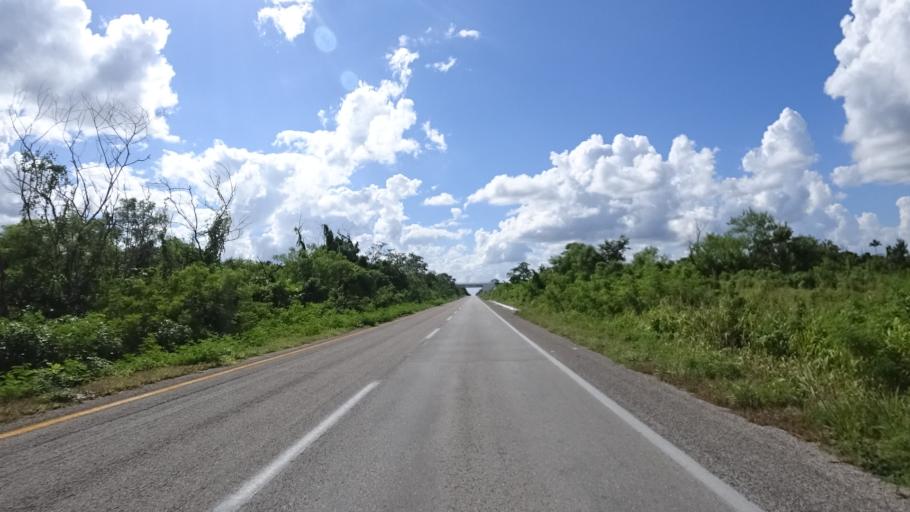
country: MX
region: Yucatan
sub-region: Kantunil
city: Kantunil
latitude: 20.7802
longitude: -88.9056
